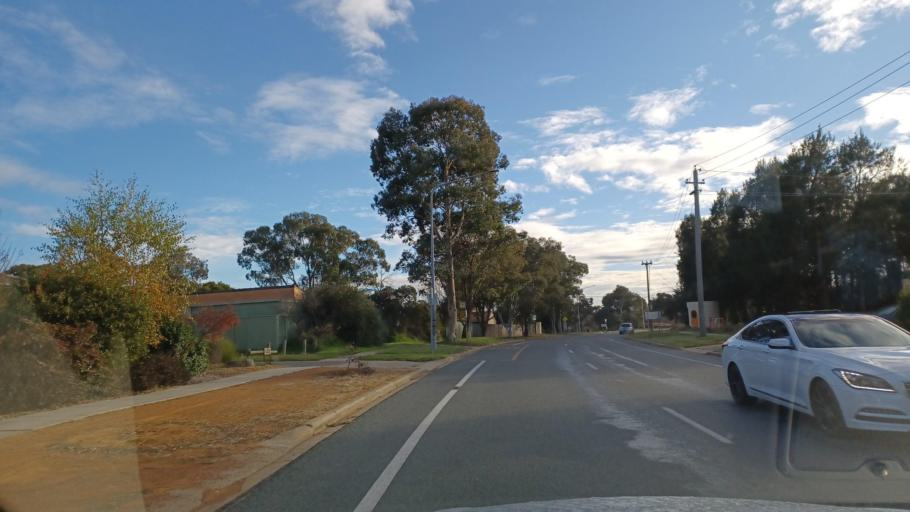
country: AU
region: Australian Capital Territory
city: Belconnen
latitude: -35.1956
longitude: 149.0415
